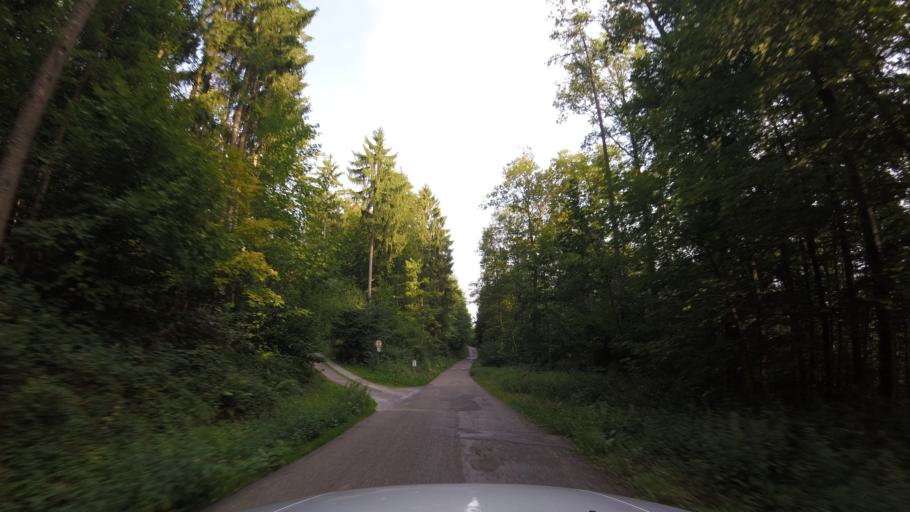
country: DE
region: Baden-Wuerttemberg
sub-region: Regierungsbezirk Stuttgart
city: Aspach
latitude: 48.9995
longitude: 9.3907
